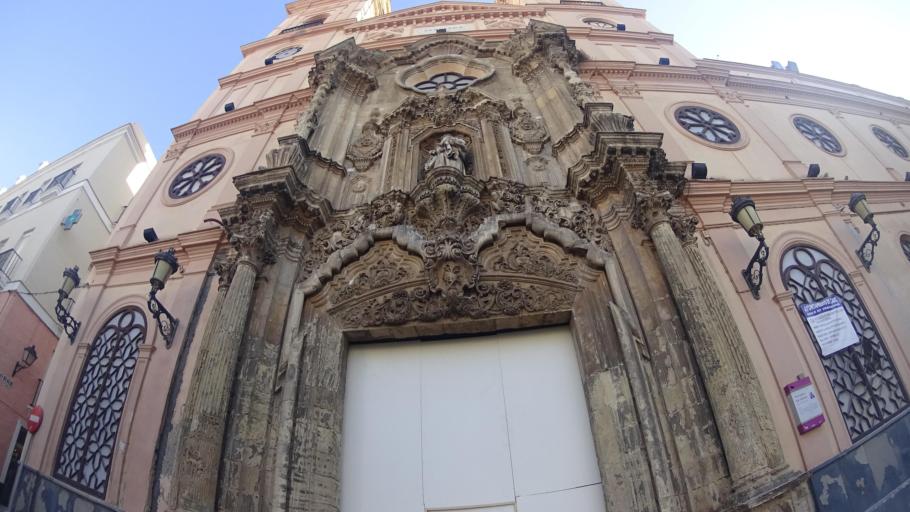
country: ES
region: Andalusia
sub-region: Provincia de Cadiz
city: Cadiz
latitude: 36.5345
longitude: -6.2992
